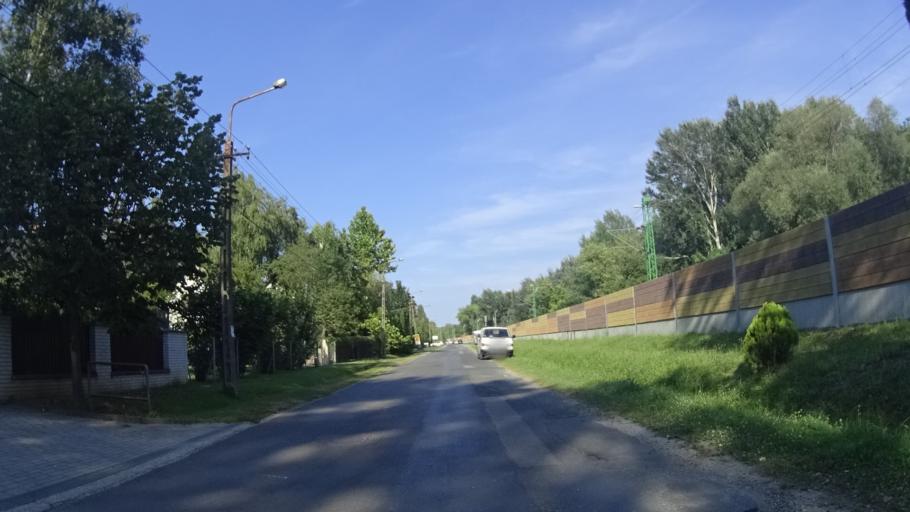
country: HU
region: Somogy
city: Balatonszarszo
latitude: 46.8370
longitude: 17.8431
